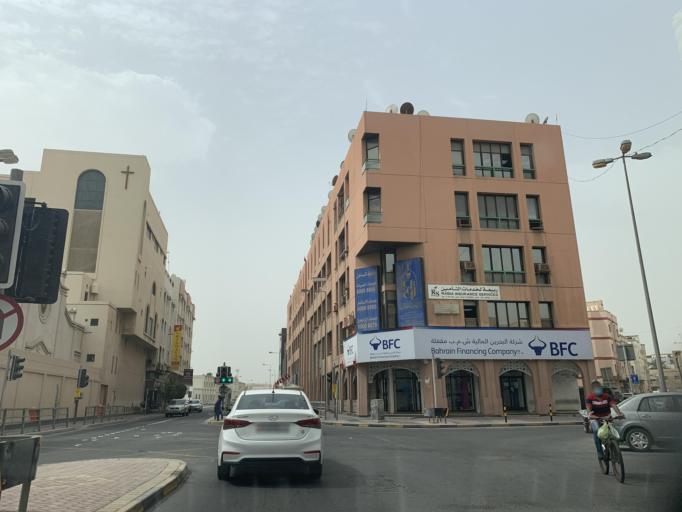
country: BH
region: Manama
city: Manama
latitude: 26.2277
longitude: 50.5795
